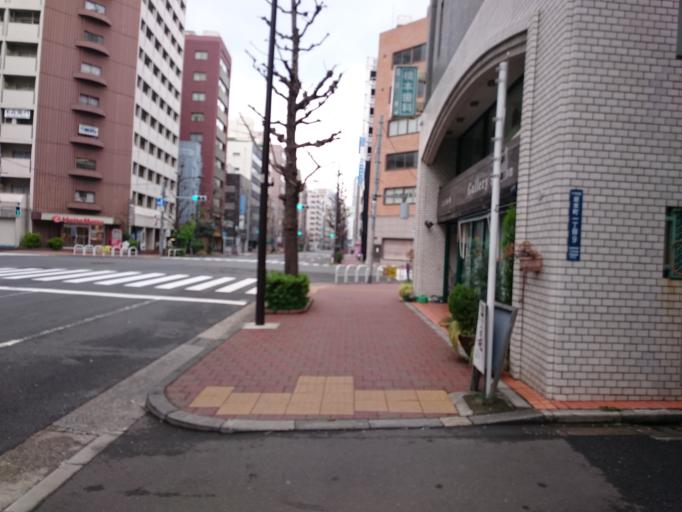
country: JP
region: Tokyo
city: Tokyo
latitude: 35.6923
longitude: 139.7774
